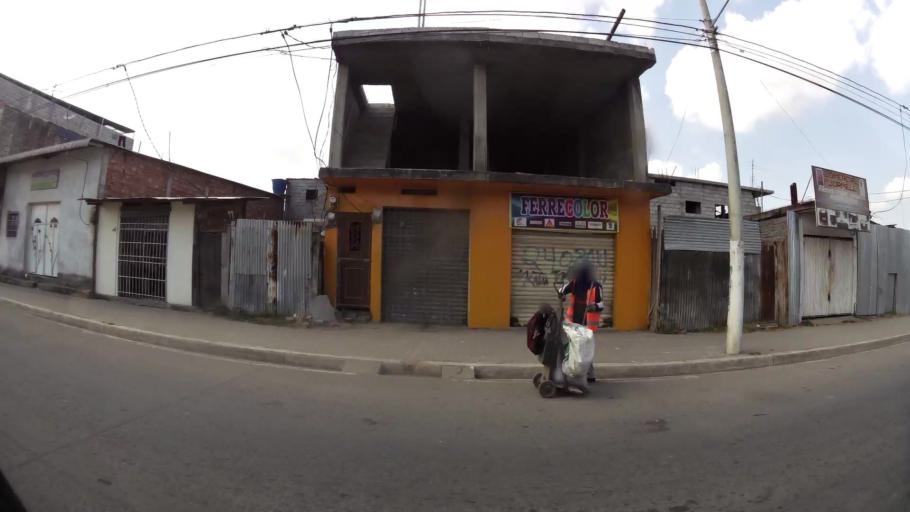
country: EC
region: Guayas
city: Eloy Alfaro
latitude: -2.1634
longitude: -79.8349
